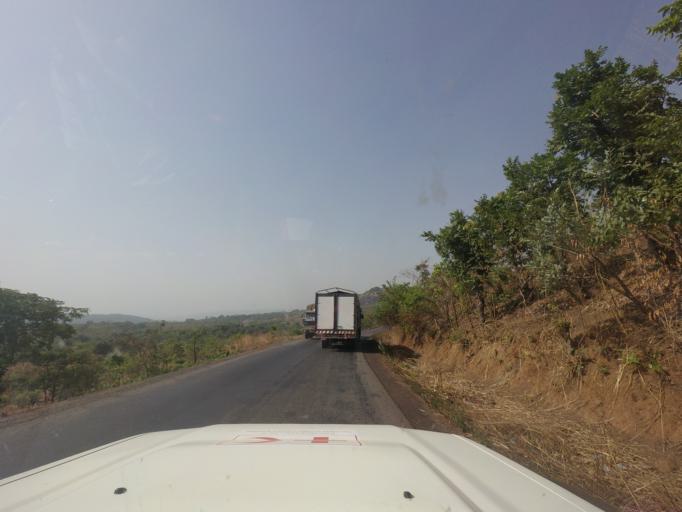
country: GN
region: Mamou
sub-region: Mamou Prefecture
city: Mamou
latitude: 10.2466
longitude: -12.4571
